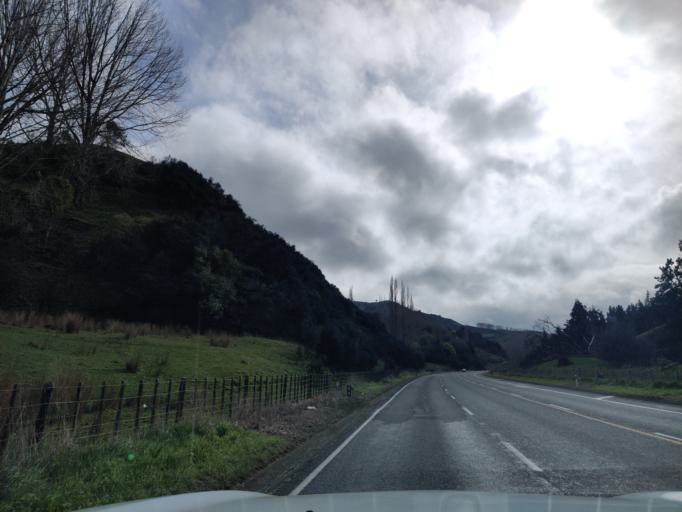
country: NZ
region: Manawatu-Wanganui
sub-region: Ruapehu District
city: Waiouru
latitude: -39.7813
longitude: 175.7864
